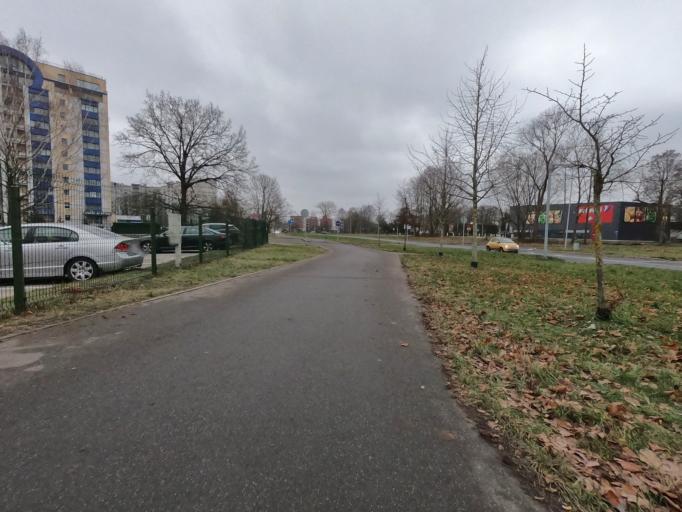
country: LV
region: Marupe
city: Marupe
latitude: 56.9461
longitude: 24.0131
